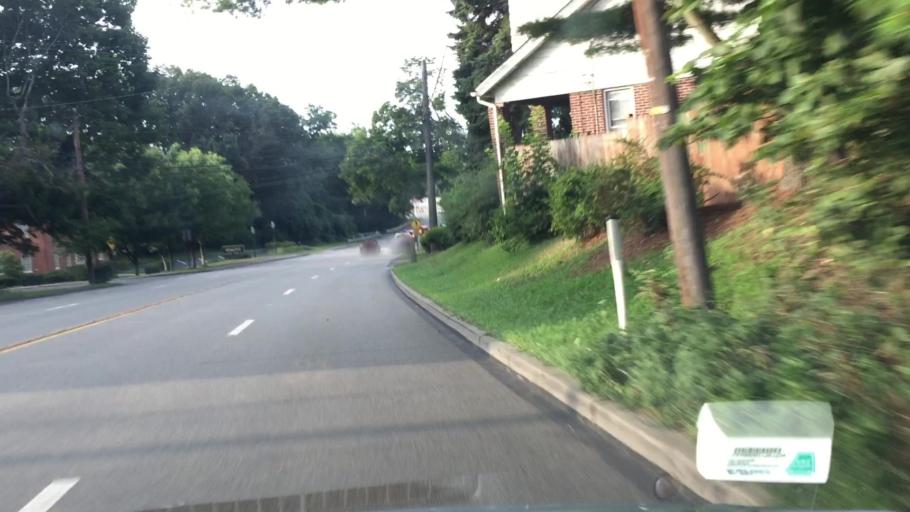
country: US
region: Pennsylvania
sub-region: Allegheny County
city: West View
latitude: 40.5508
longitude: -80.0373
